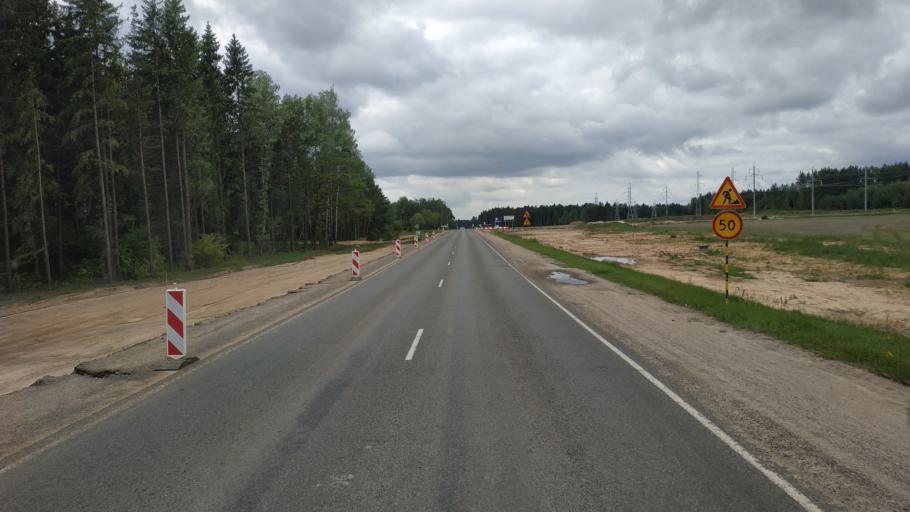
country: BY
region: Mogilev
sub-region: Mahilyowski Rayon
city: Veyno
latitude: 53.8745
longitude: 30.4363
